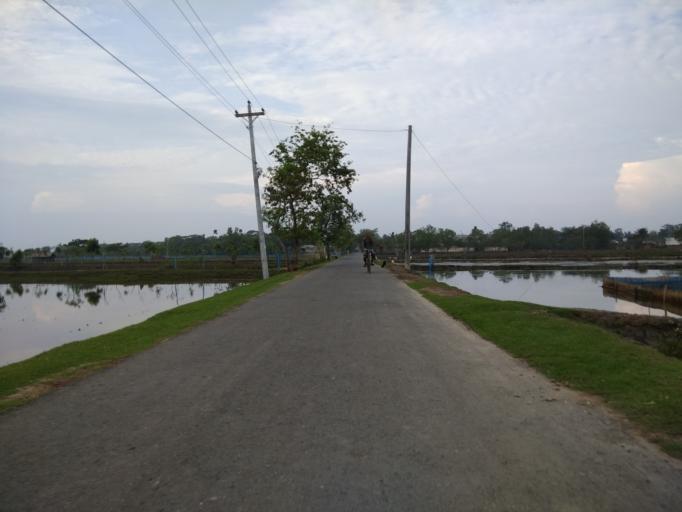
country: IN
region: West Bengal
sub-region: North 24 Parganas
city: Taki
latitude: 22.2841
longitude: 89.2025
